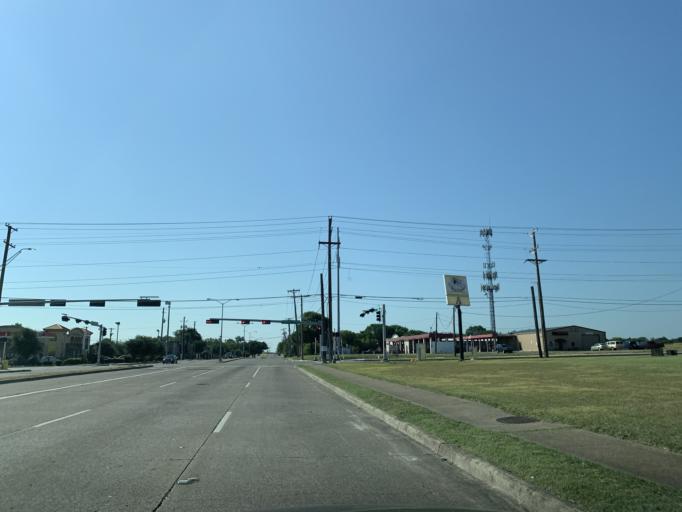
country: US
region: Texas
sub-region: Dallas County
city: Hutchins
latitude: 32.6732
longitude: -96.7634
